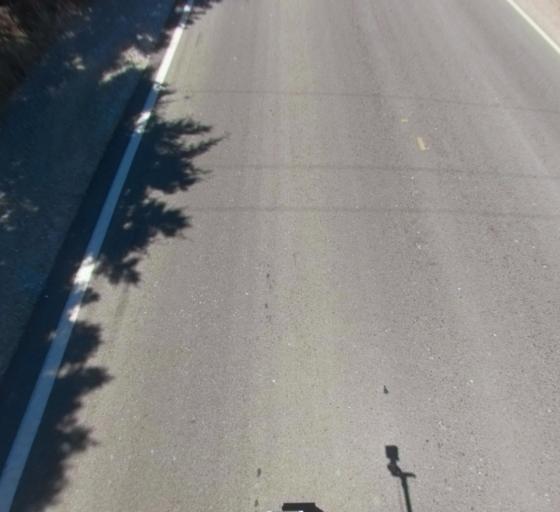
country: US
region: California
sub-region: Madera County
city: Bonadelle Ranchos-Madera Ranchos
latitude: 36.8924
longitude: -119.8935
